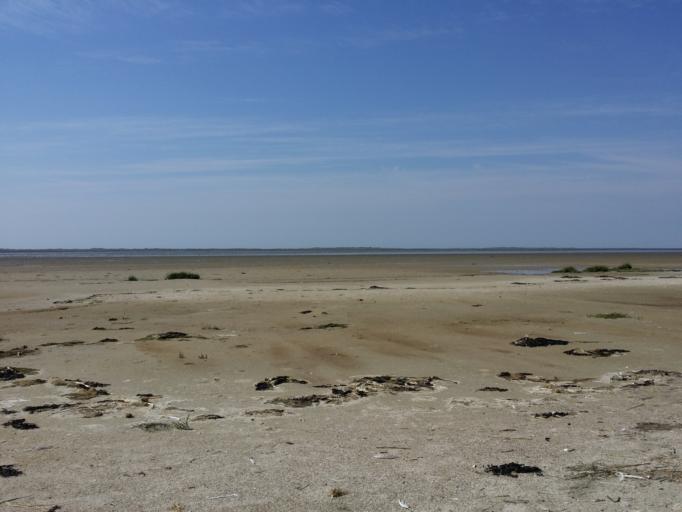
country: DK
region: South Denmark
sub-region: Fano Kommune
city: Nordby
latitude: 55.5138
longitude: 8.3070
